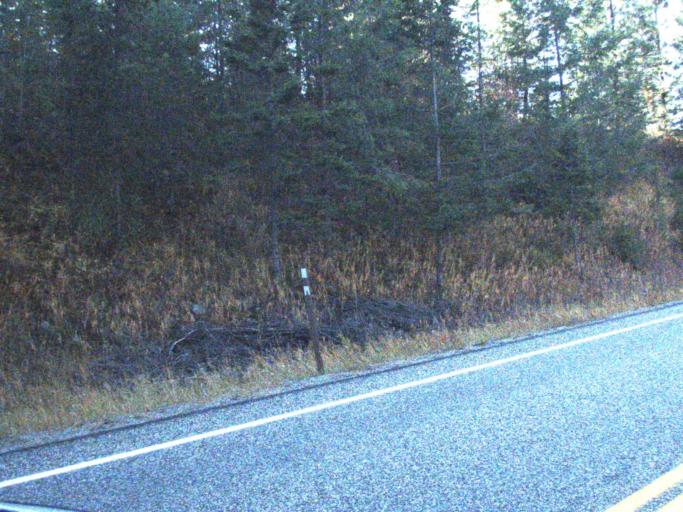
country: CA
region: British Columbia
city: Rossland
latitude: 48.9588
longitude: -117.8018
